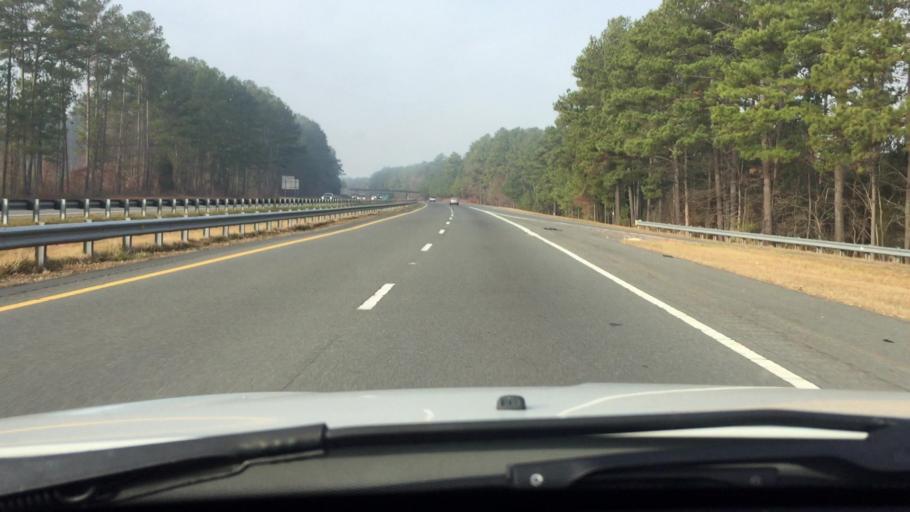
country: US
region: North Carolina
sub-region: Wake County
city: Green Level
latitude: 35.6447
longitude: -79.0075
